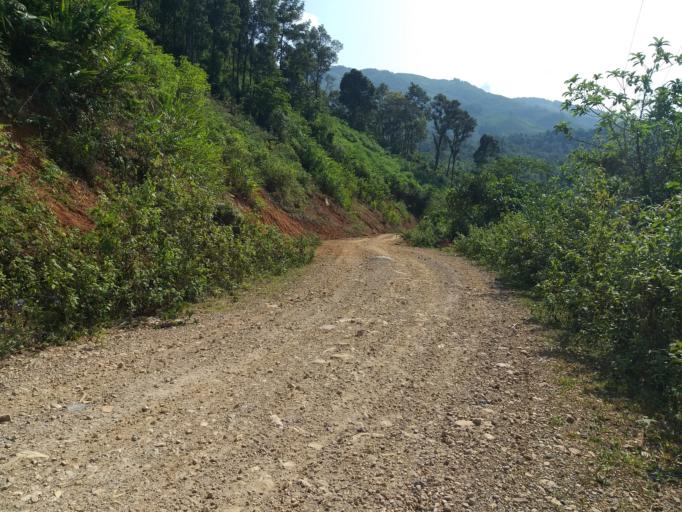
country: LA
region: Phongsali
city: Khoa
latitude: 21.2113
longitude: 102.6099
